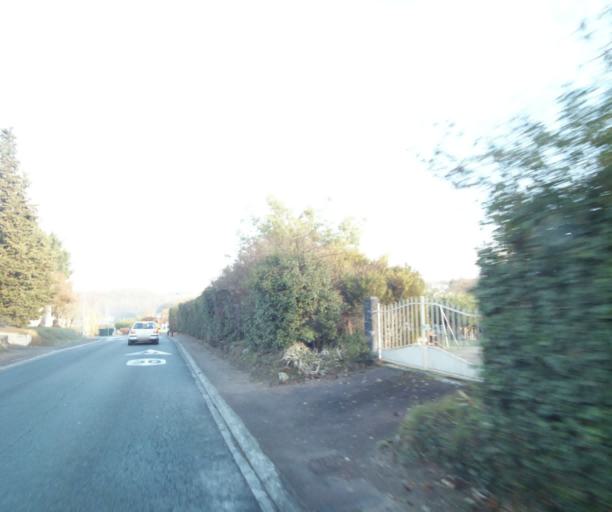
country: FR
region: Poitou-Charentes
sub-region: Departement de la Charente-Maritime
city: Fontcouverte
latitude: 45.7695
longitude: -0.5906
